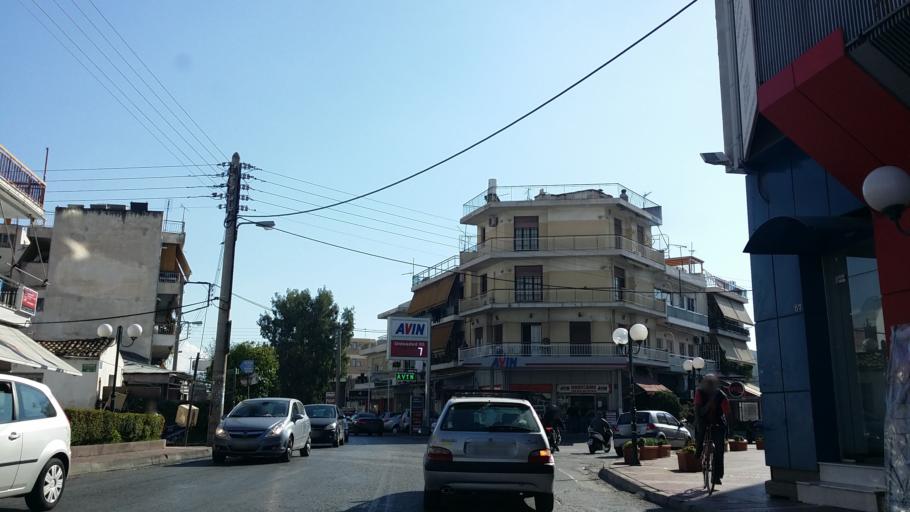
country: GR
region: Attica
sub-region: Nomarchia Athinas
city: Peristeri
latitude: 38.0150
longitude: 23.7078
